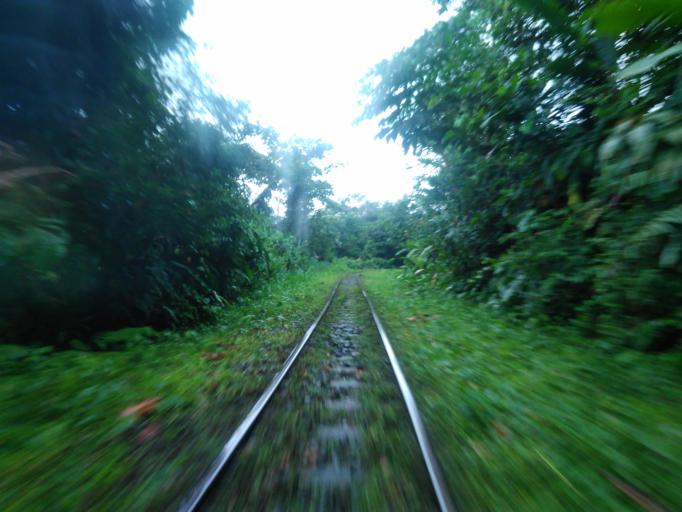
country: CO
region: Valle del Cauca
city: Buenaventura
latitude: 3.8450
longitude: -76.8692
